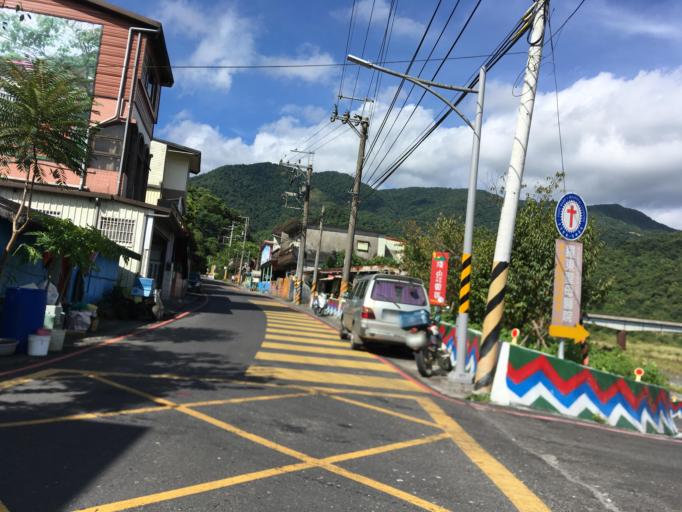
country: TW
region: Taiwan
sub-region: Yilan
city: Yilan
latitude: 24.6105
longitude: 121.6878
